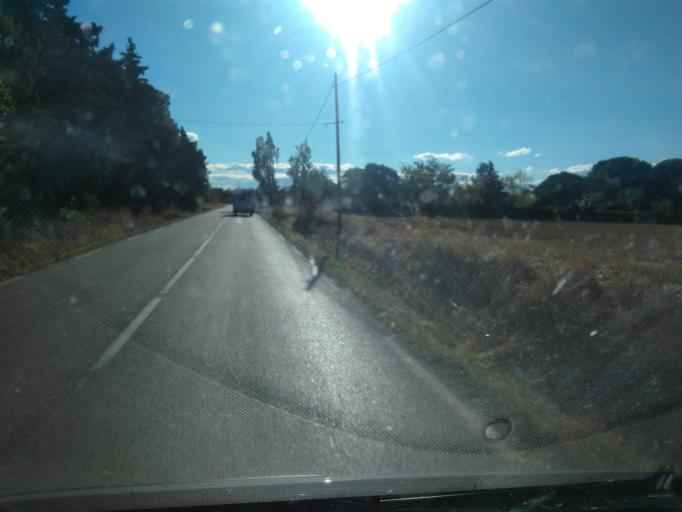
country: FR
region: Languedoc-Roussillon
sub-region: Departement du Gard
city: Vauvert
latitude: 43.6902
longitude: 4.2607
